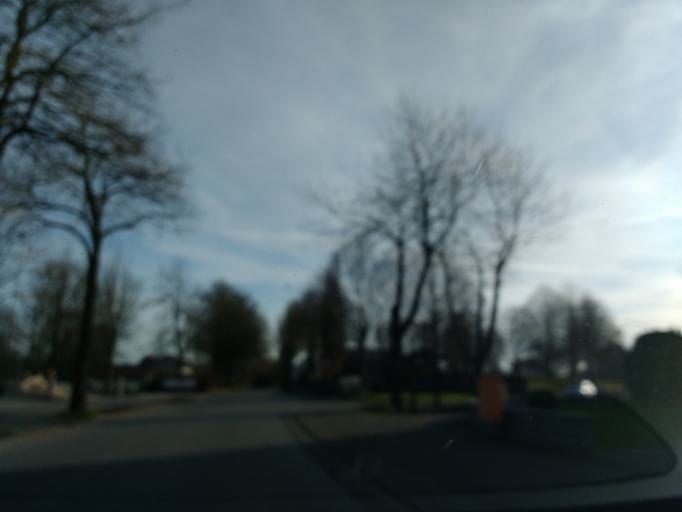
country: DE
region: North Rhine-Westphalia
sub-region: Regierungsbezirk Detmold
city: Salzkotten
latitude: 51.6589
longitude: 8.6016
